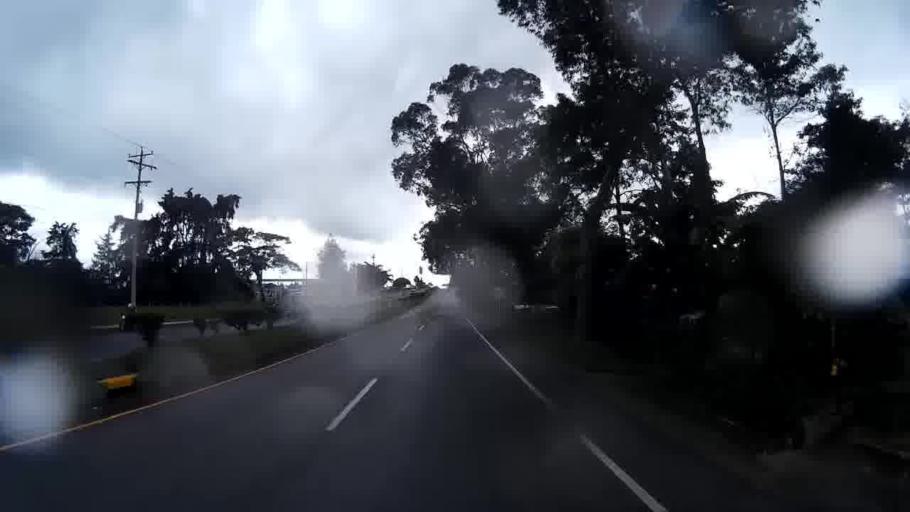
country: CO
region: Quindio
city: Circasia
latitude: 4.6251
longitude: -75.6204
